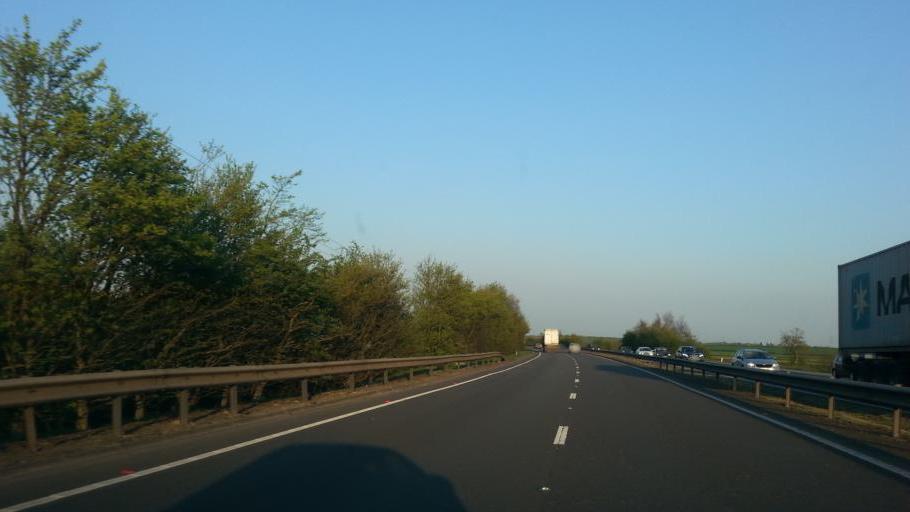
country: GB
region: England
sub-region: Bedford
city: Swineshead
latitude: 52.3665
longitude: -0.4485
